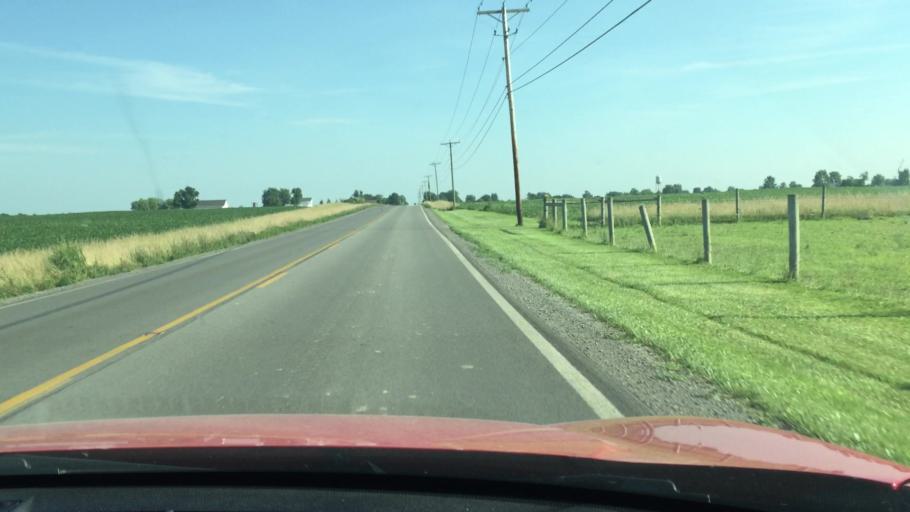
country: US
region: Ohio
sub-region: Hardin County
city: Ada
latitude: 40.7248
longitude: -83.8423
